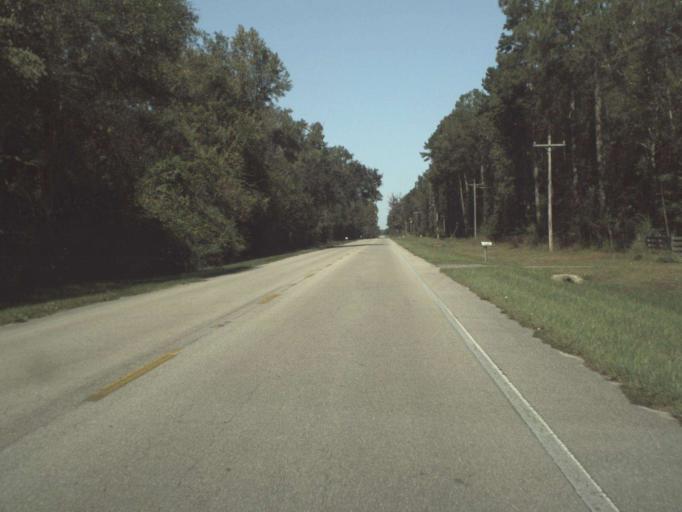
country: US
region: Florida
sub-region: Jefferson County
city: Monticello
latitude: 30.3840
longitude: -84.0078
